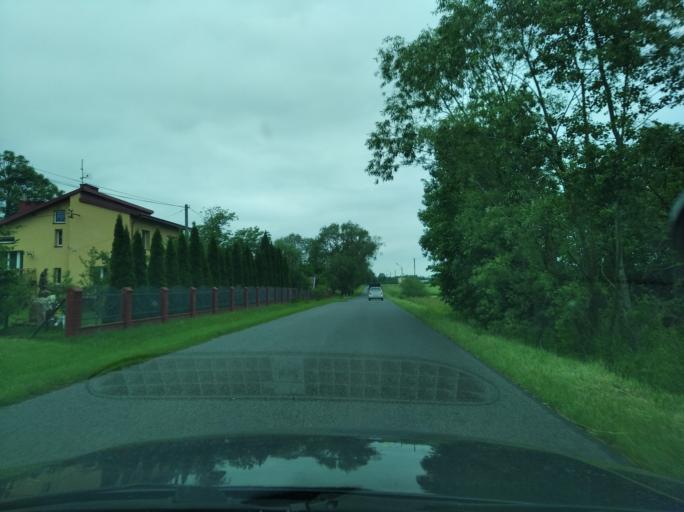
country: PL
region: Subcarpathian Voivodeship
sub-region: Powiat kolbuszowski
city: Niwiska
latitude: 50.1676
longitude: 21.6688
